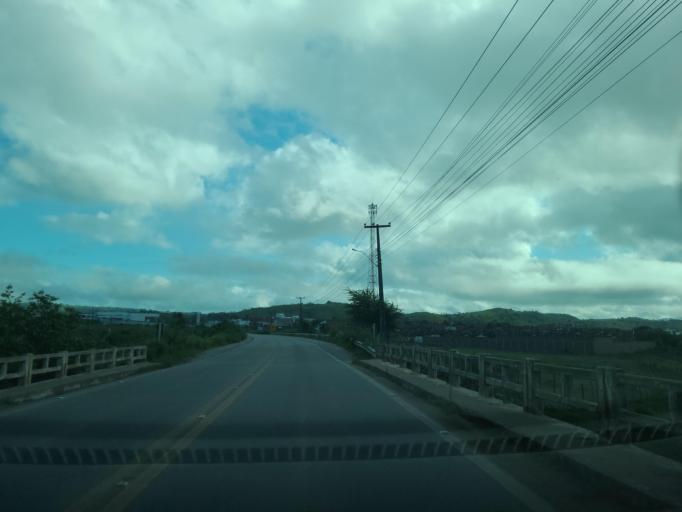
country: BR
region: Alagoas
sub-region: Uniao Dos Palmares
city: Uniao dos Palmares
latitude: -9.1551
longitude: -36.0135
